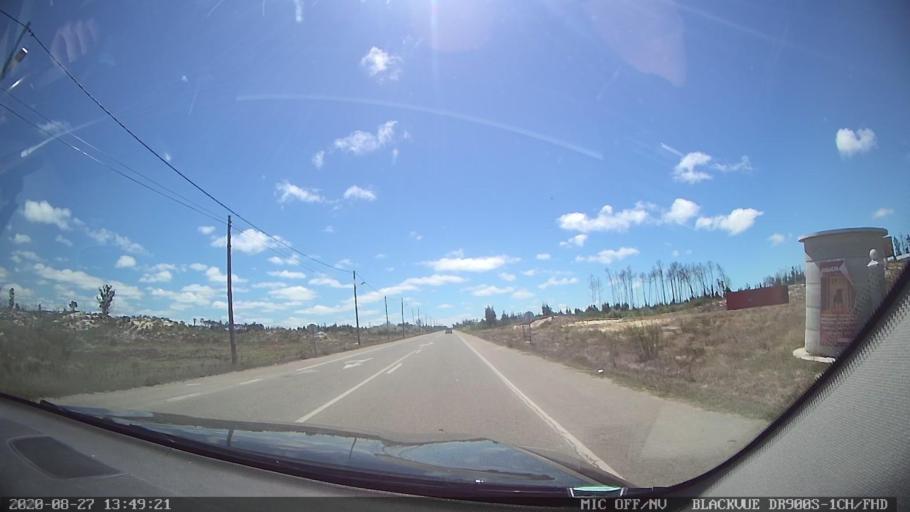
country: PT
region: Coimbra
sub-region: Mira
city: Mira
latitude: 40.3688
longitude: -8.7464
